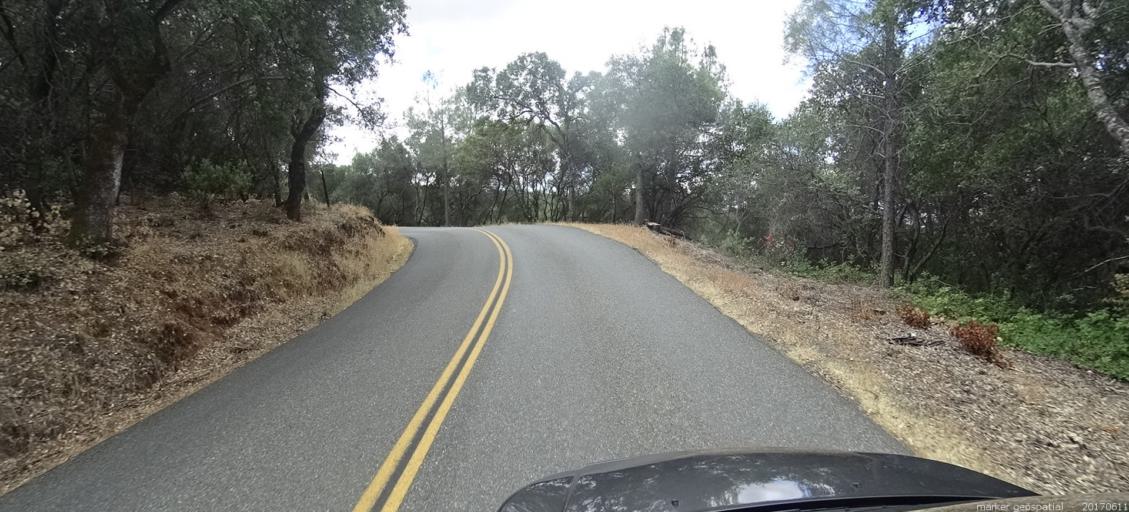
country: US
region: California
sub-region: Butte County
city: Paradise
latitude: 39.6484
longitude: -121.5485
